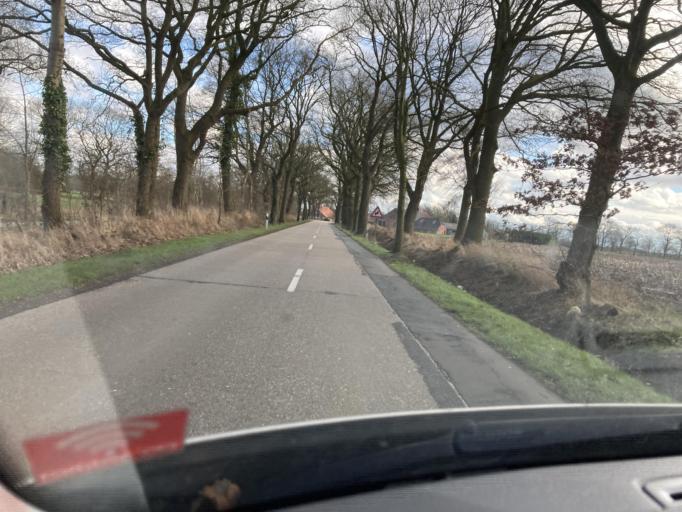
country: DE
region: Lower Saxony
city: Filsum
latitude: 53.2387
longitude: 7.6501
